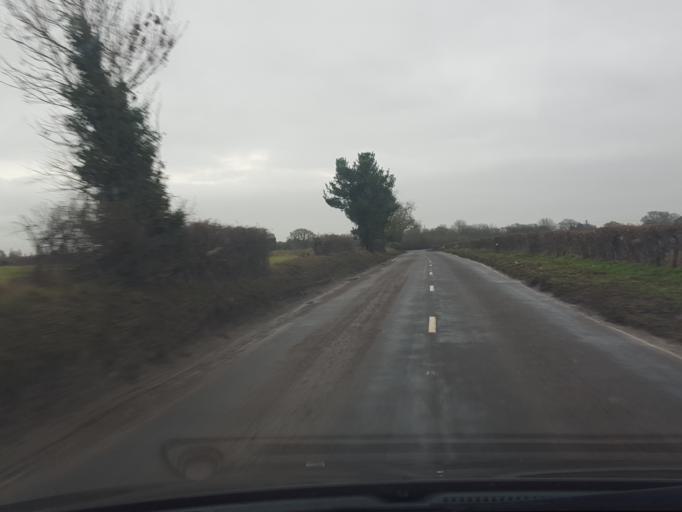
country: GB
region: England
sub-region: Essex
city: Alresford
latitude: 51.9173
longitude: 0.9905
